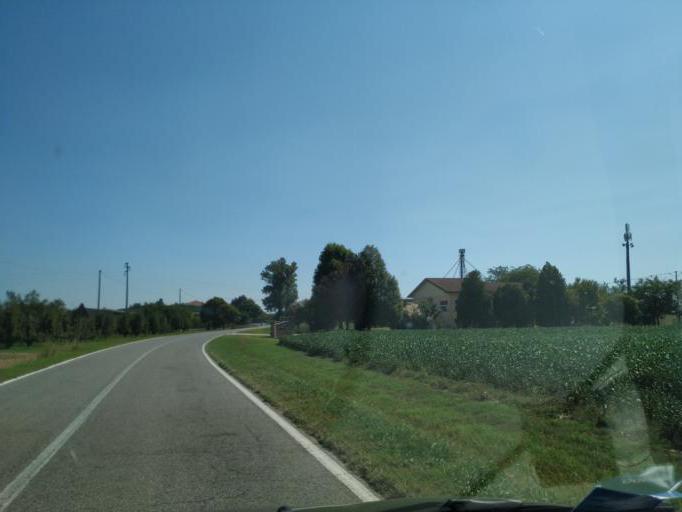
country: IT
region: Emilia-Romagna
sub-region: Provincia di Ferrara
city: Coccanile-Cesta
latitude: 44.9121
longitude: 11.9007
